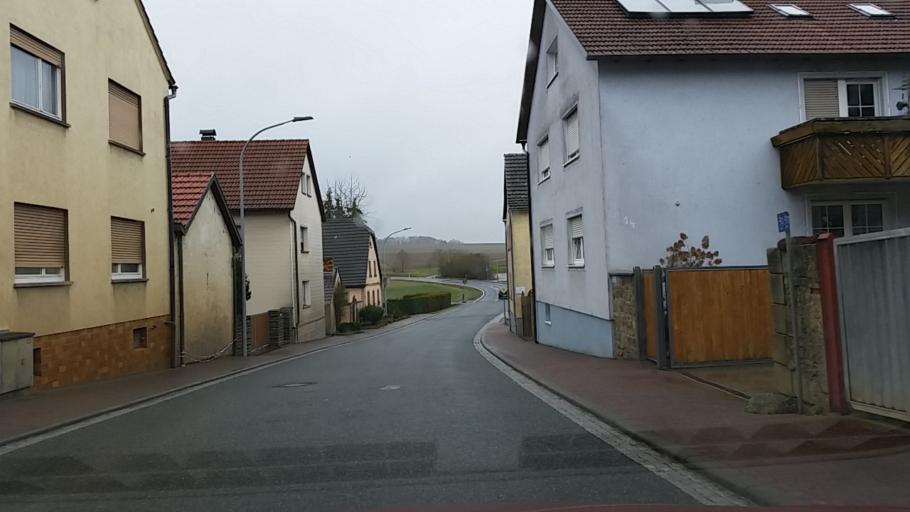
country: DE
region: Bavaria
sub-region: Regierungsbezirk Unterfranken
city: Arnstein
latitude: 49.9283
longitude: 9.9685
